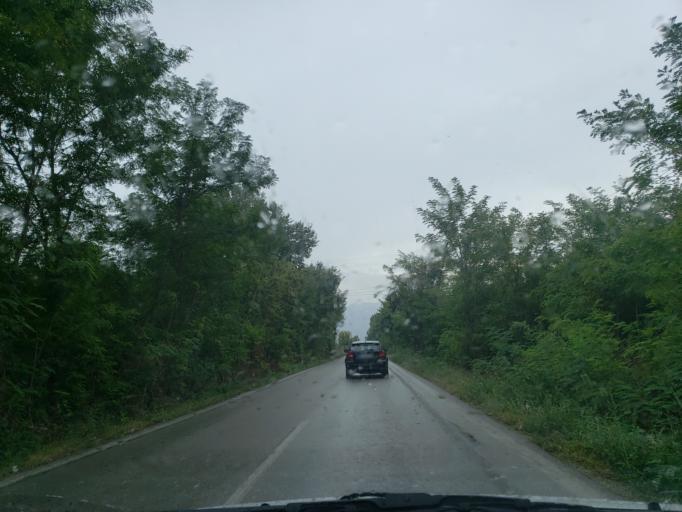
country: GR
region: Central Greece
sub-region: Nomos Fthiotidos
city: Anthili
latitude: 38.8469
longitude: 22.4407
